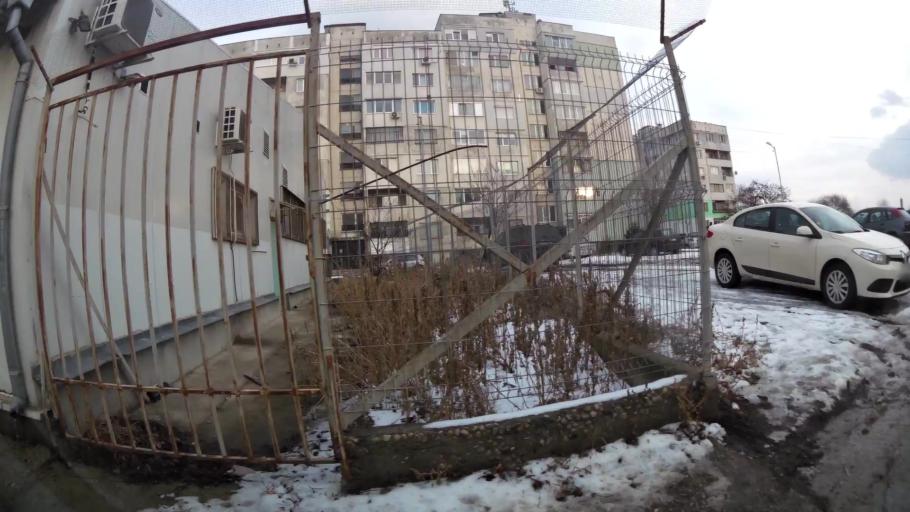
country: BG
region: Sofia-Capital
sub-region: Stolichna Obshtina
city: Sofia
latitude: 42.7221
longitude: 23.3480
